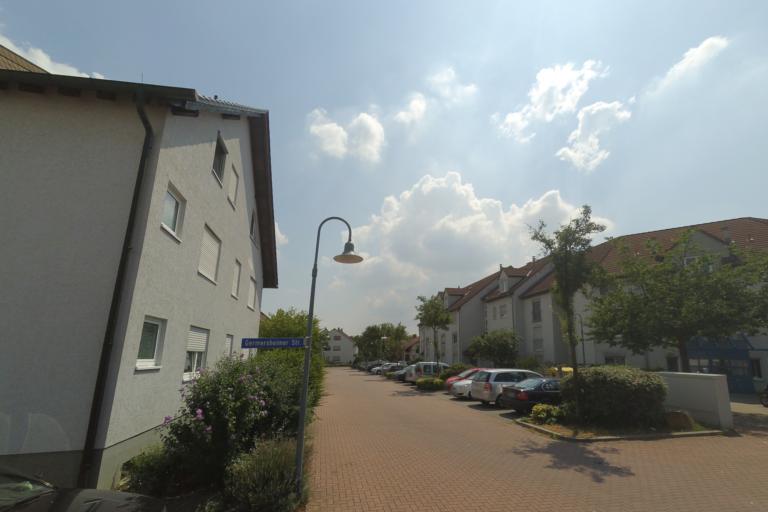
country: DE
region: Rheinland-Pfalz
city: Gartenstadt
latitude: 49.4527
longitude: 8.3823
